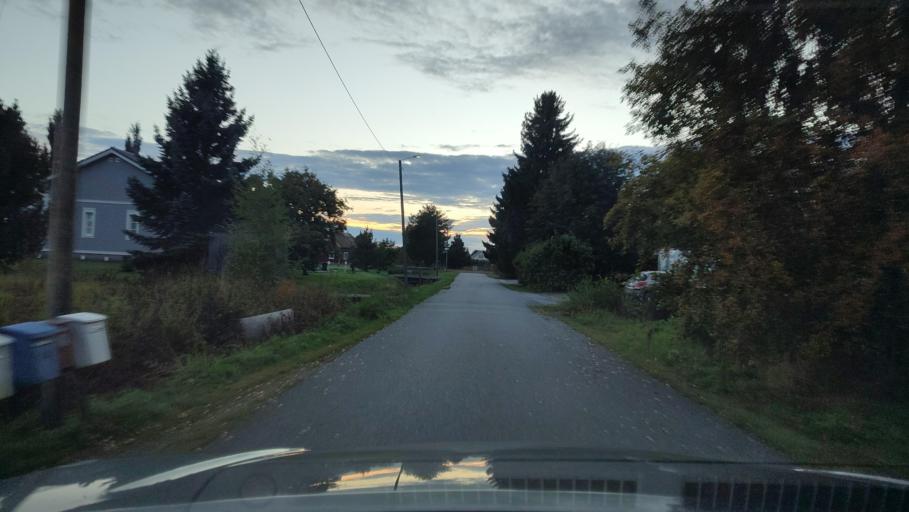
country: FI
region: Ostrobothnia
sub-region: Sydosterbotten
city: Kristinestad
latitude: 62.2513
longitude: 21.5146
